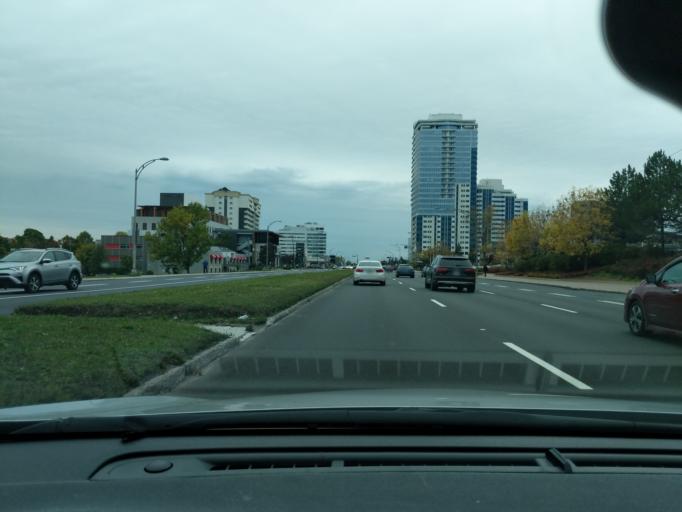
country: CA
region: Quebec
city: L'Ancienne-Lorette
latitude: 46.7696
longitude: -71.2839
